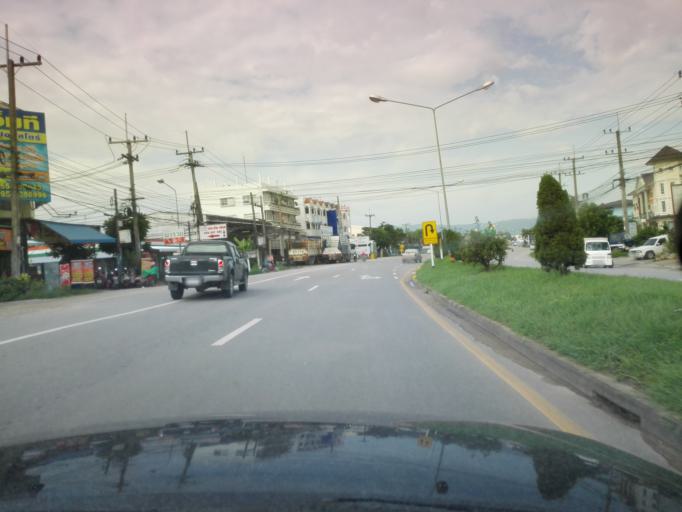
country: TH
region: Tak
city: Mae Sot
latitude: 16.7213
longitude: 98.5644
